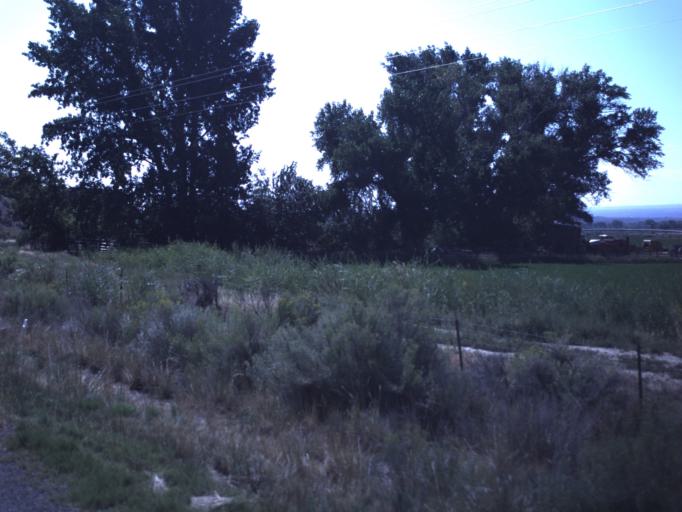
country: US
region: Utah
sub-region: Duchesne County
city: Duchesne
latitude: 40.2703
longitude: -110.4229
